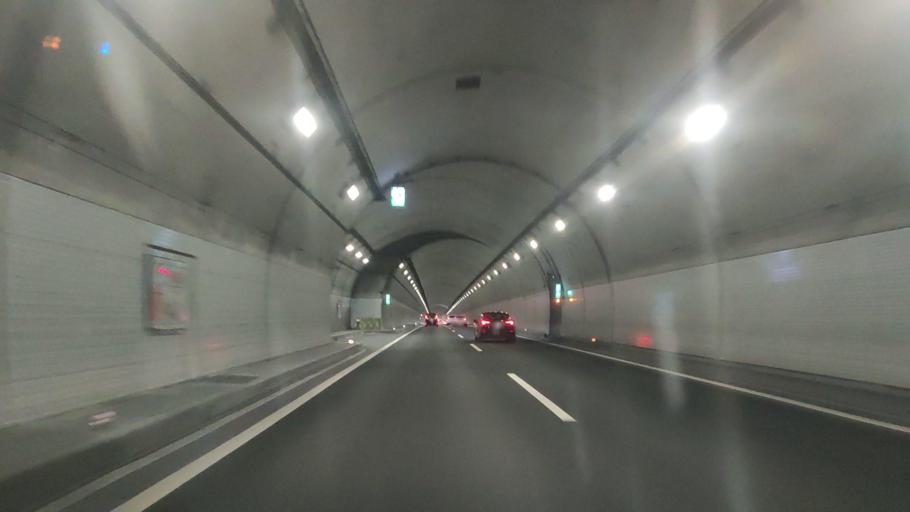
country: JP
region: Fukuoka
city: Kanda
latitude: 33.8091
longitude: 130.9148
